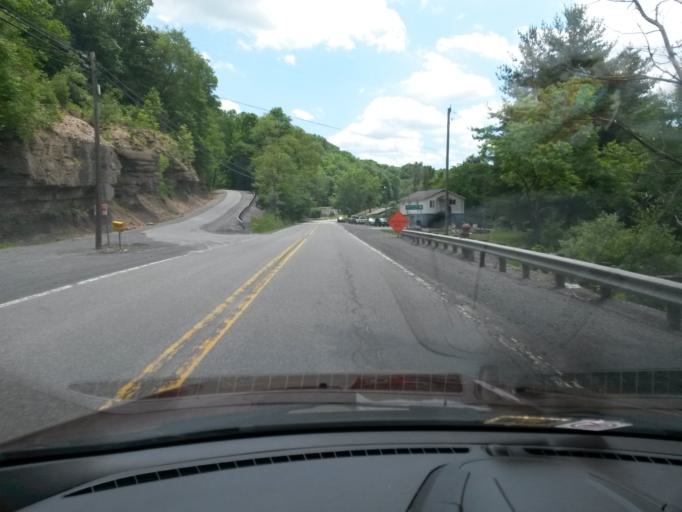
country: US
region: West Virginia
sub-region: Greenbrier County
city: Rainelle
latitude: 38.0467
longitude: -80.7220
